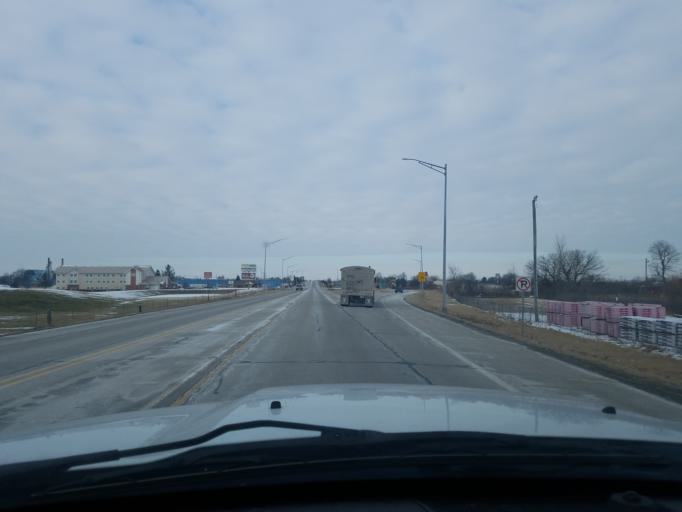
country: US
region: Indiana
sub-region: Randolph County
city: Winchester
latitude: 40.1674
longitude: -84.9669
